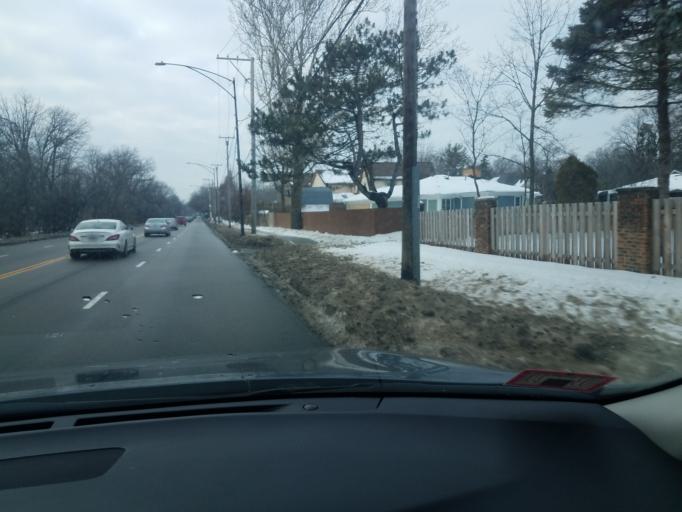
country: US
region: Illinois
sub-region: Cook County
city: Niles
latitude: 42.0018
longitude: -87.7761
